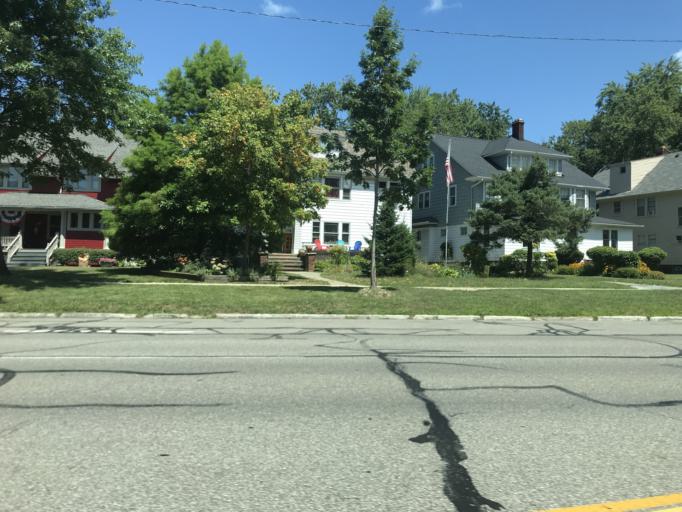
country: US
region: Ohio
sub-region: Cuyahoga County
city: Lakewood
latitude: 41.4902
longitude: -81.7797
